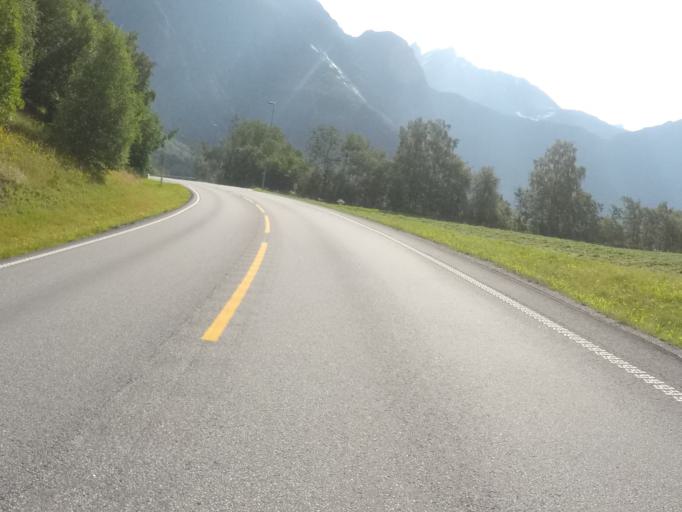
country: NO
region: More og Romsdal
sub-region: Rauma
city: Andalsnes
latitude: 62.5331
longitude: 7.7328
